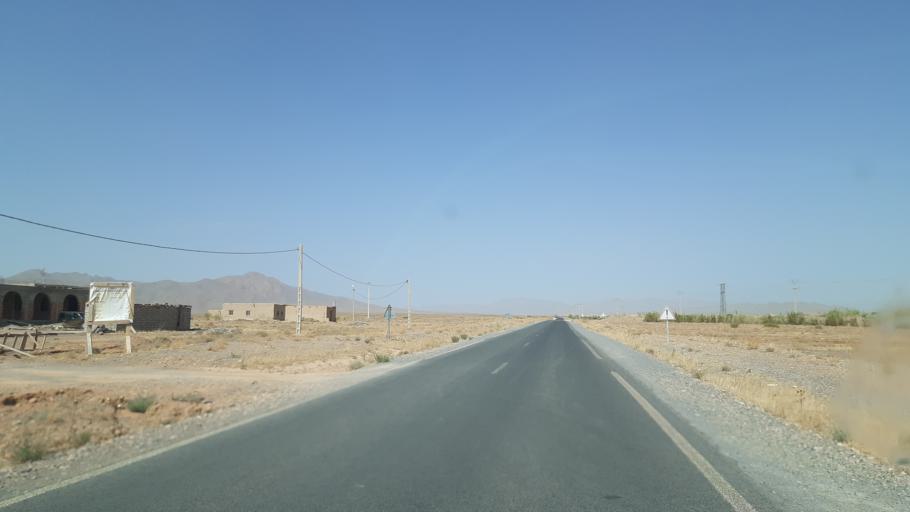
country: MA
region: Meknes-Tafilalet
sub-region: Errachidia
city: Amouguer
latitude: 32.2372
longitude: -4.6201
